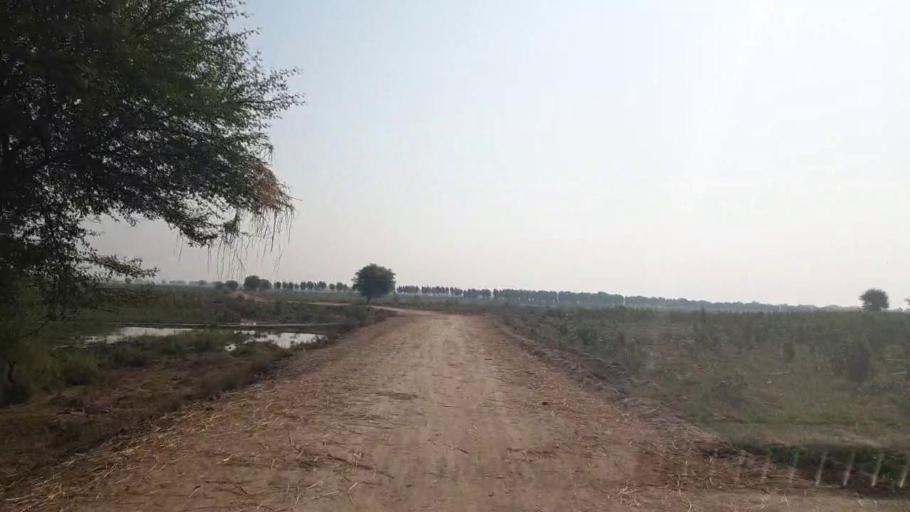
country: PK
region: Sindh
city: Sehwan
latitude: 26.4512
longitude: 67.8325
